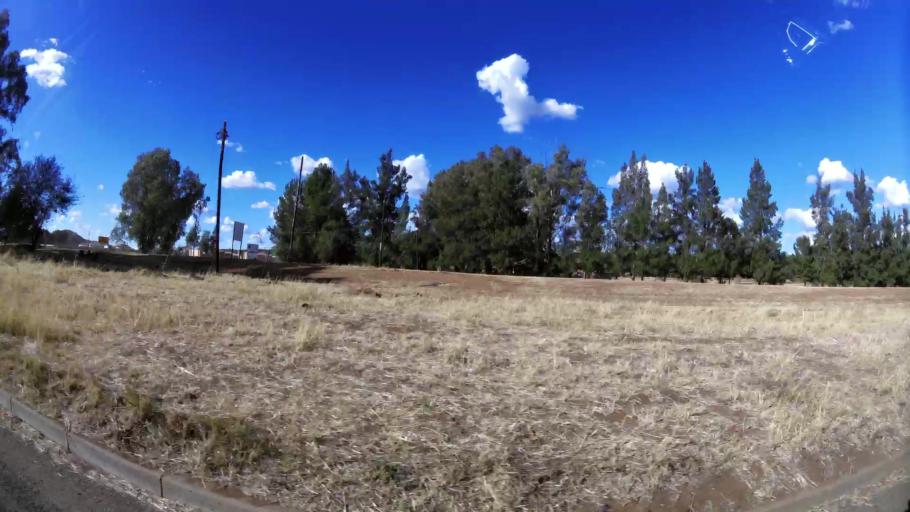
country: ZA
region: North-West
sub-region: Dr Kenneth Kaunda District Municipality
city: Klerksdorp
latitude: -26.8188
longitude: 26.6657
